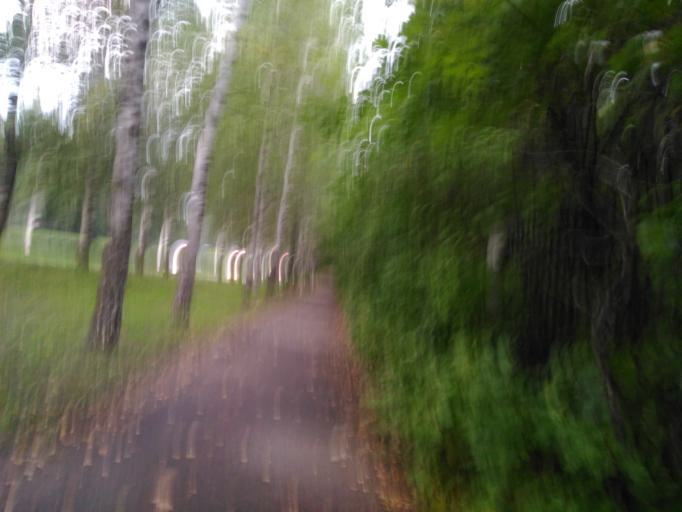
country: RU
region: Ulyanovsk
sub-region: Ulyanovskiy Rayon
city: Ulyanovsk
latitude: 54.2696
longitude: 48.3349
